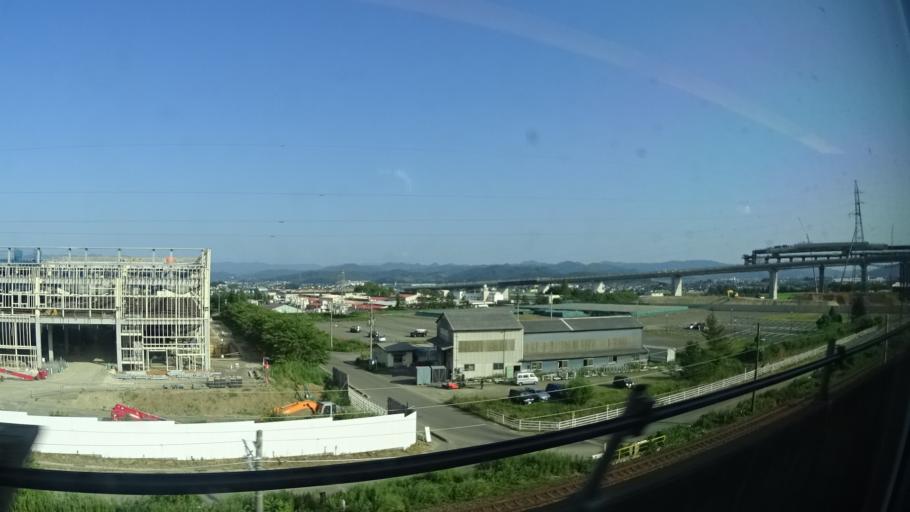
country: JP
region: Fukushima
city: Hobaramachi
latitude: 37.8371
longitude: 140.5031
